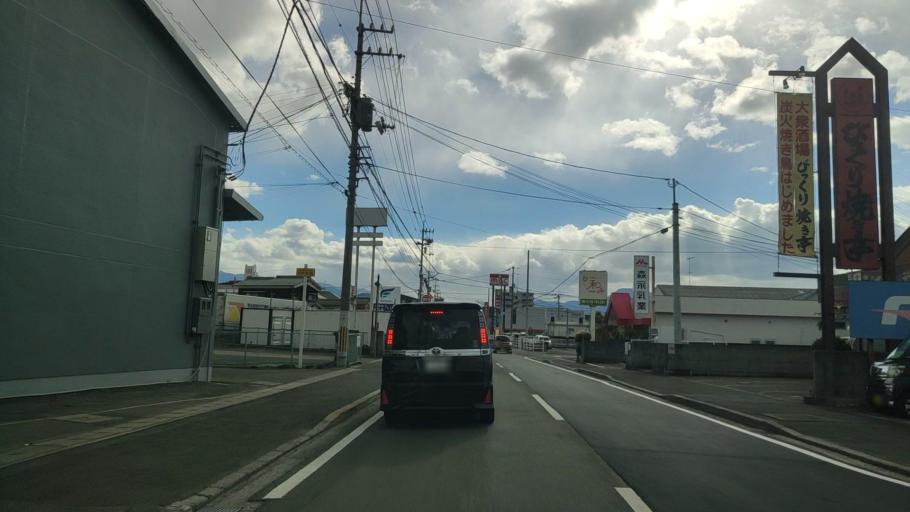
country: JP
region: Ehime
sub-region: Shikoku-chuo Shi
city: Matsuyama
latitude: 33.8115
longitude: 132.7952
